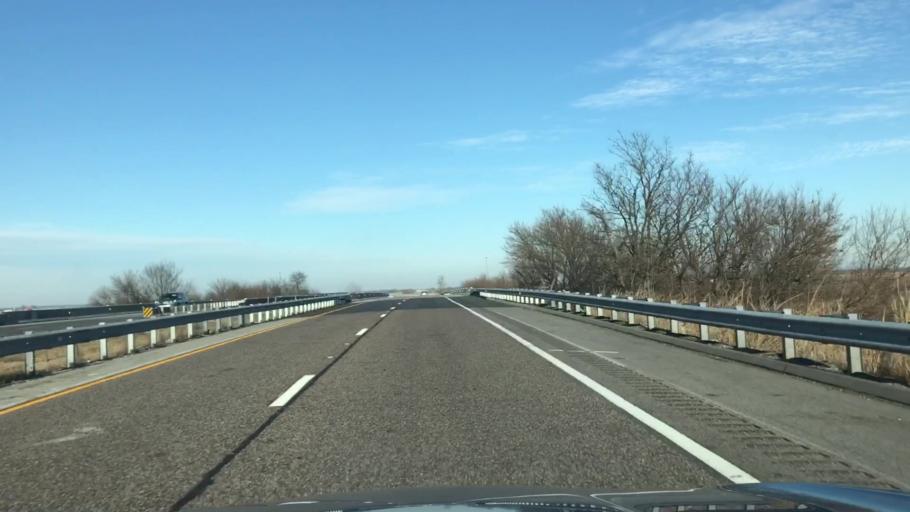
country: US
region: Illinois
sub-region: Madison County
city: Edwardsville
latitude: 38.8245
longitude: -89.8834
